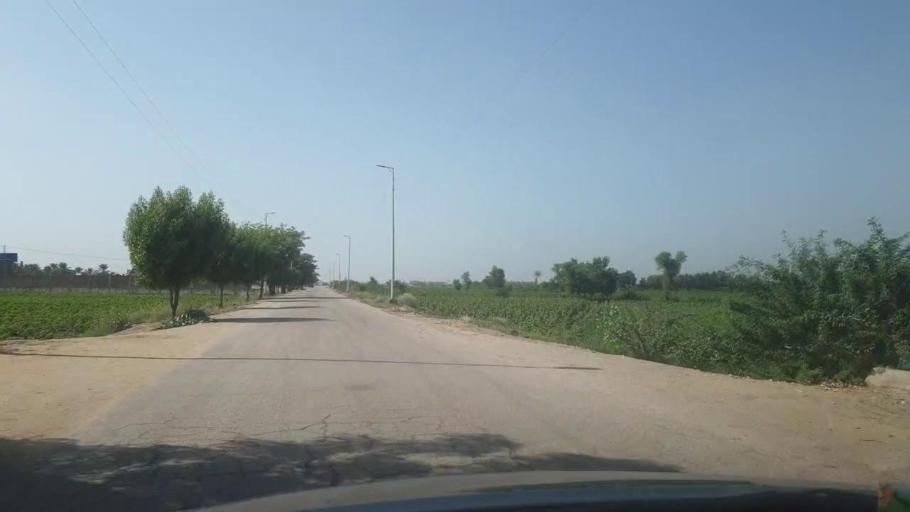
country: PK
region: Sindh
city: Rohri
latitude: 27.5093
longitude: 69.0362
